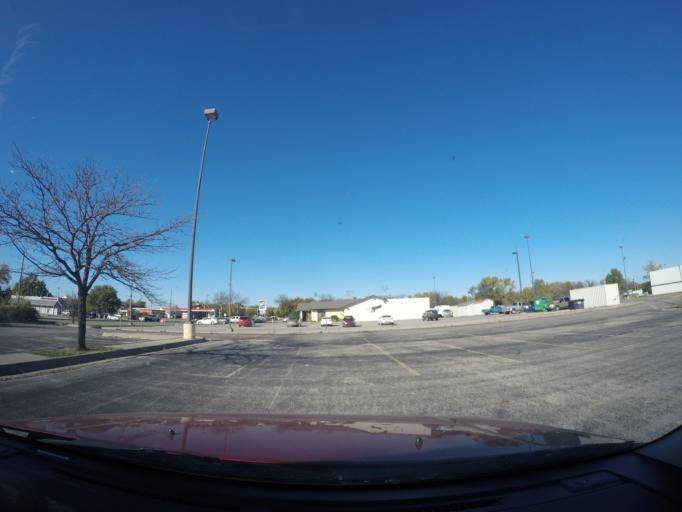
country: US
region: Kansas
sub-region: Sedgwick County
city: Wichita
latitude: 37.6791
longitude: -97.3935
